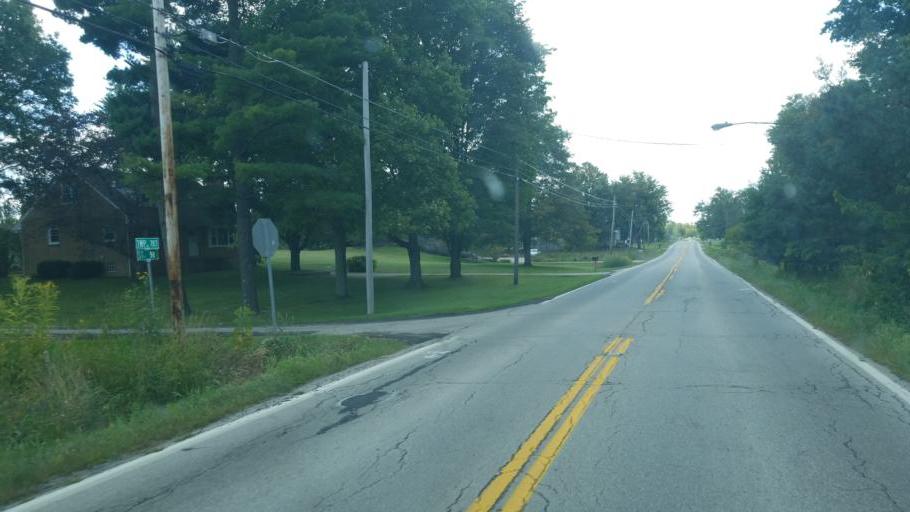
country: US
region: Ohio
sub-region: Ashland County
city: Ashland
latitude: 40.9175
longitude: -82.2815
